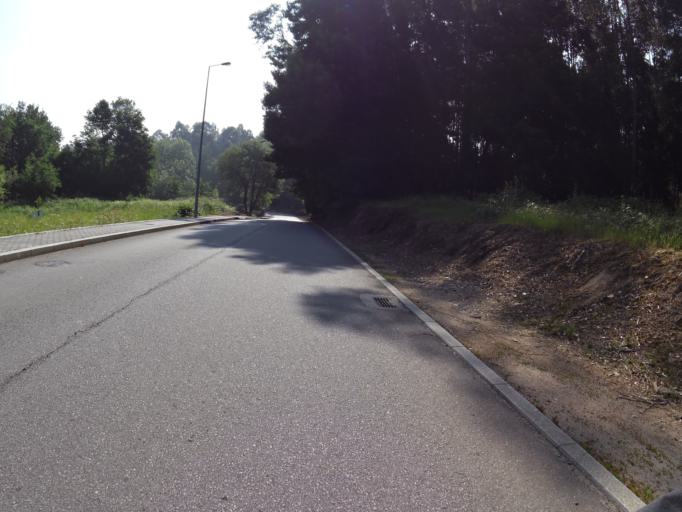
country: PT
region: Aveiro
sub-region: Santa Maria da Feira
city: Argoncilhe
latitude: 41.0338
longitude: -8.5475
